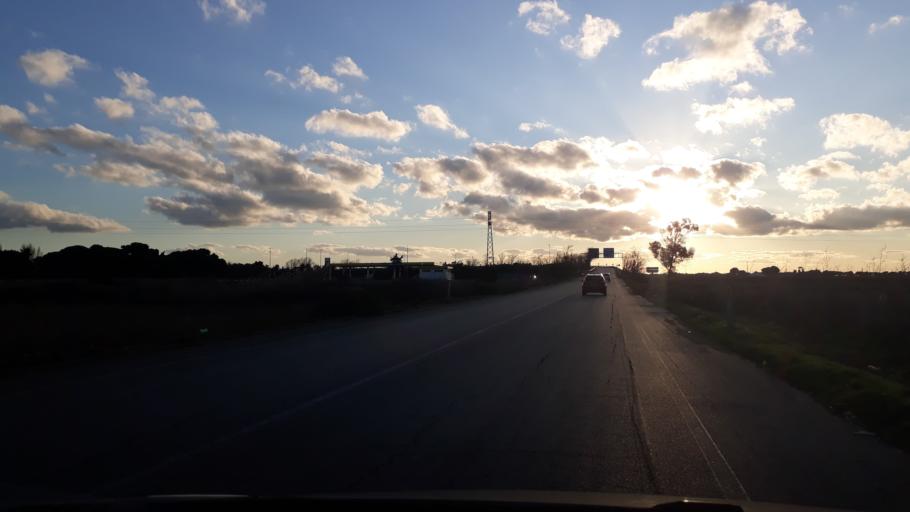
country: IT
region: Apulia
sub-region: Provincia di Brindisi
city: Brindisi
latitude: 40.6557
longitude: 17.8963
